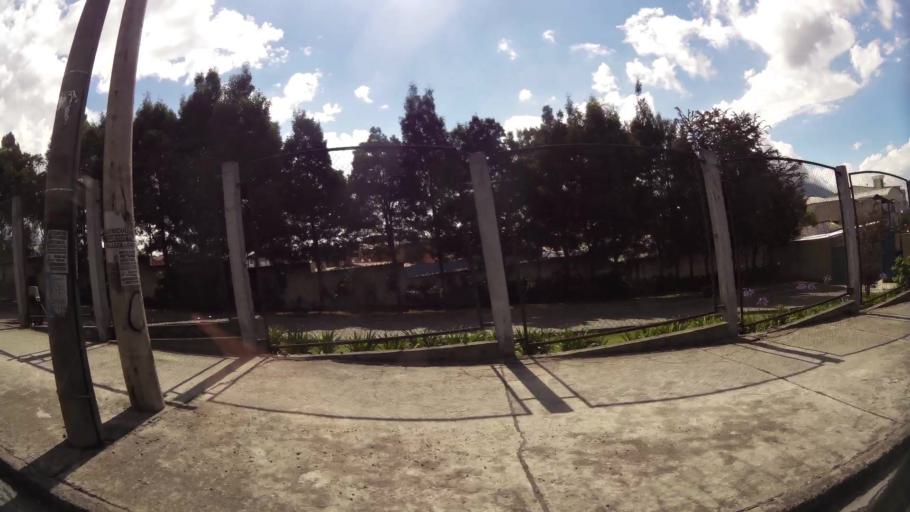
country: EC
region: Pichincha
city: Quito
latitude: -0.1061
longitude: -78.4727
